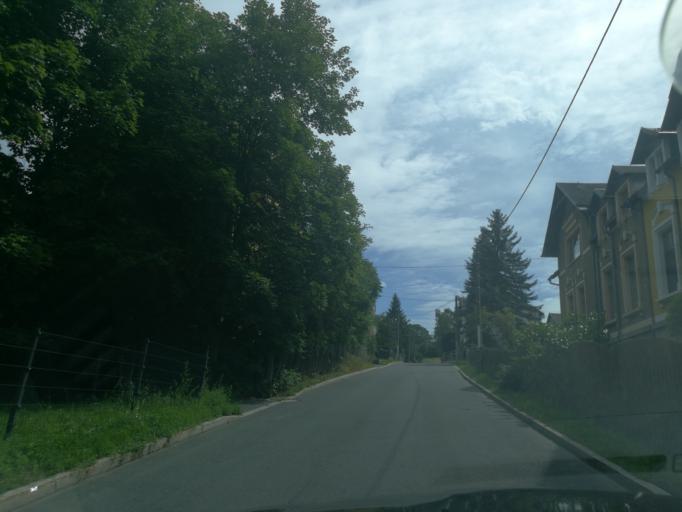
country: DE
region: Saxony
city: Adorf
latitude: 50.3158
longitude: 12.2626
